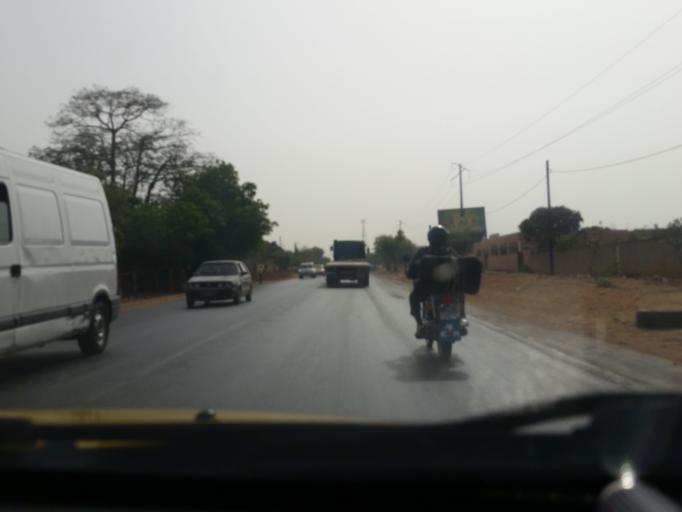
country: SN
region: Thies
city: Pout
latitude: 14.7385
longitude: -17.1432
